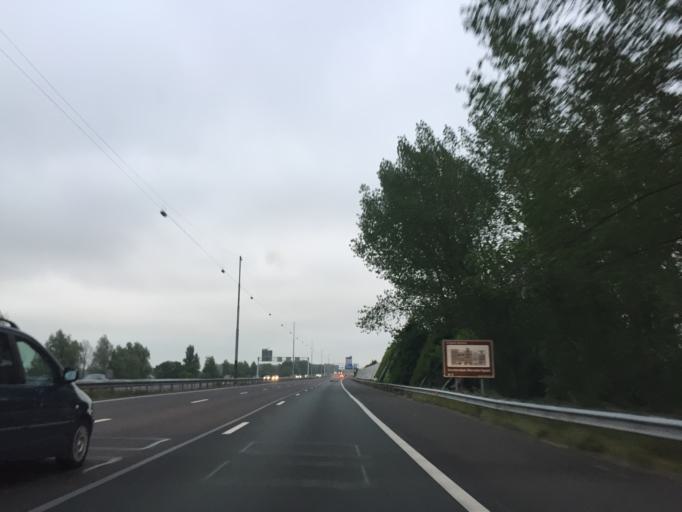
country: NL
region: North Holland
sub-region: Gemeente Landsmeer
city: Landsmeer
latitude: 52.4161
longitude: 4.9189
